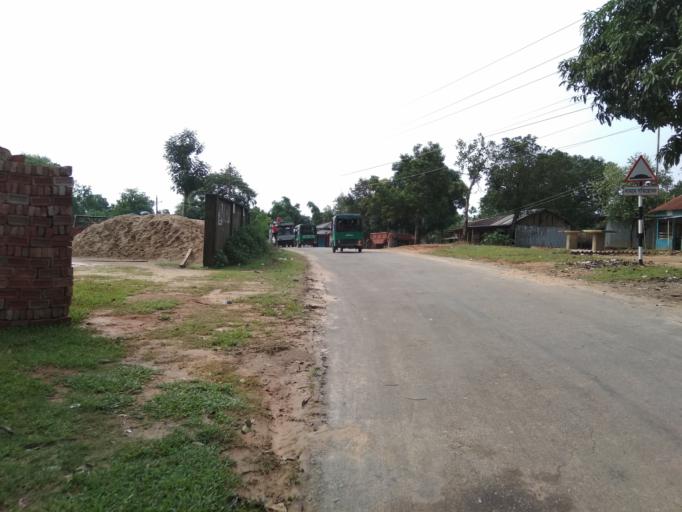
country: BD
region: Chittagong
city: Khagrachhari
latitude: 23.0004
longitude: 92.0093
